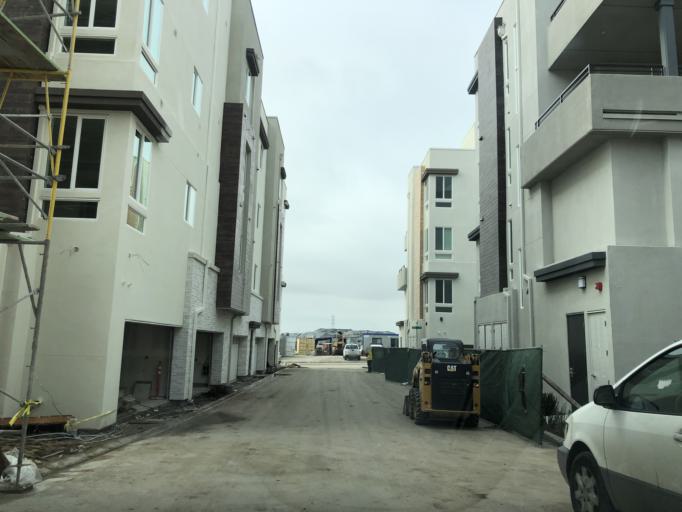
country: US
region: California
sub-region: Alameda County
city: Fremont
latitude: 37.5027
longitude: -121.9341
